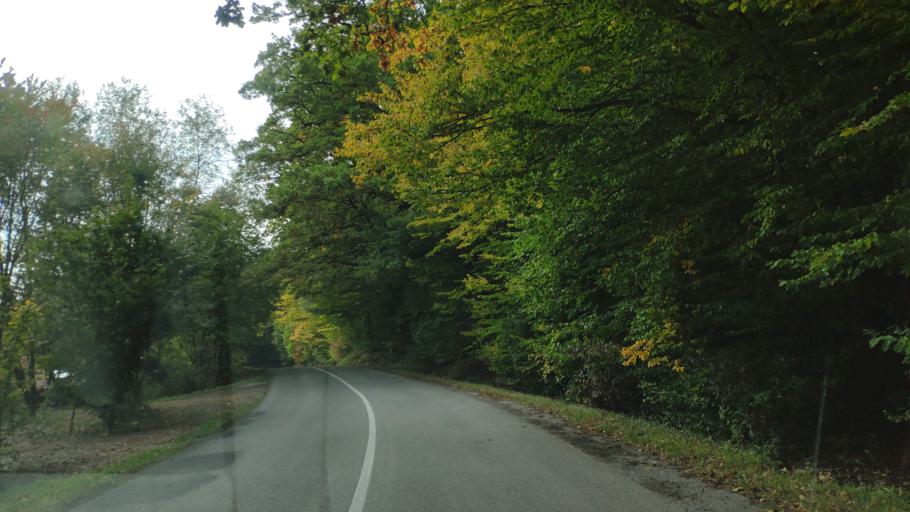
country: SK
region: Presovsky
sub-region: Okres Presov
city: Presov
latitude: 48.9535
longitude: 21.3601
